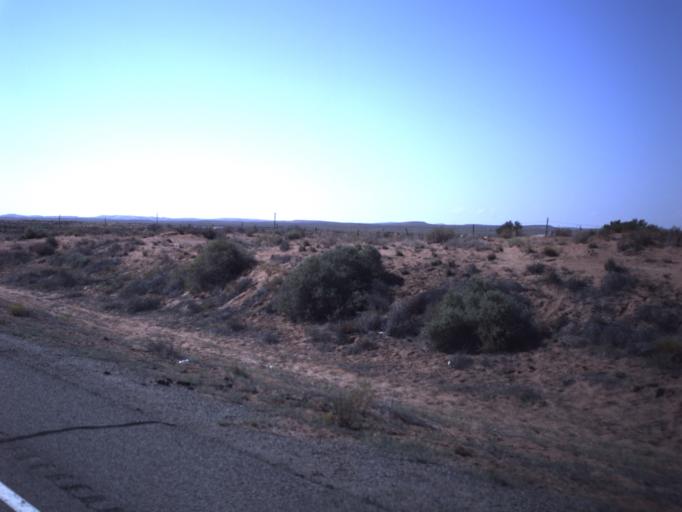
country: US
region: Utah
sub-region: San Juan County
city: Blanding
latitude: 37.2162
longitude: -109.6134
